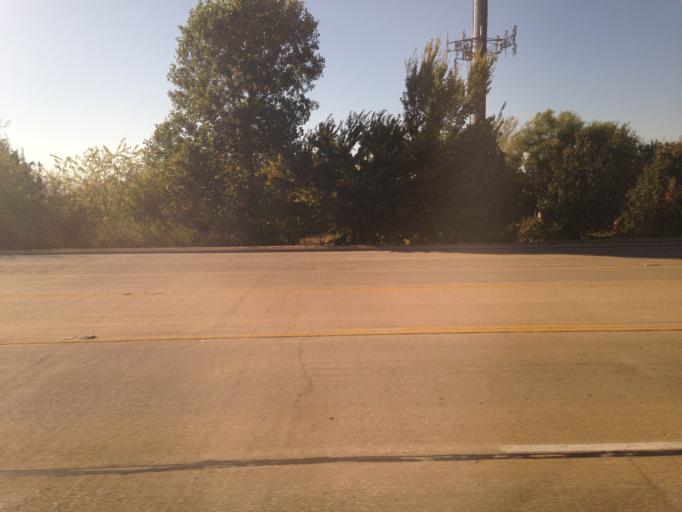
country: US
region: Texas
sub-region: Tarrant County
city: Watauga
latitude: 32.8685
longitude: -97.2628
